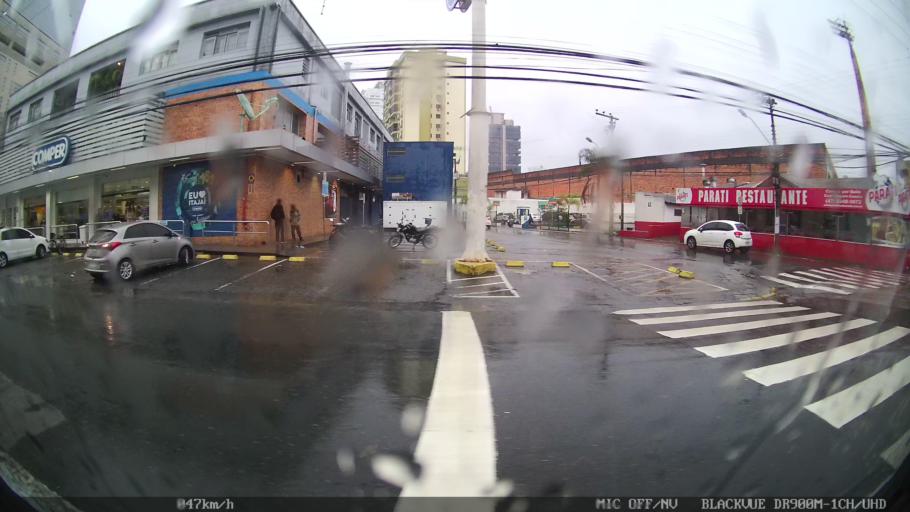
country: BR
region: Santa Catarina
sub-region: Itajai
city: Itajai
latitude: -26.9082
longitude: -48.6586
